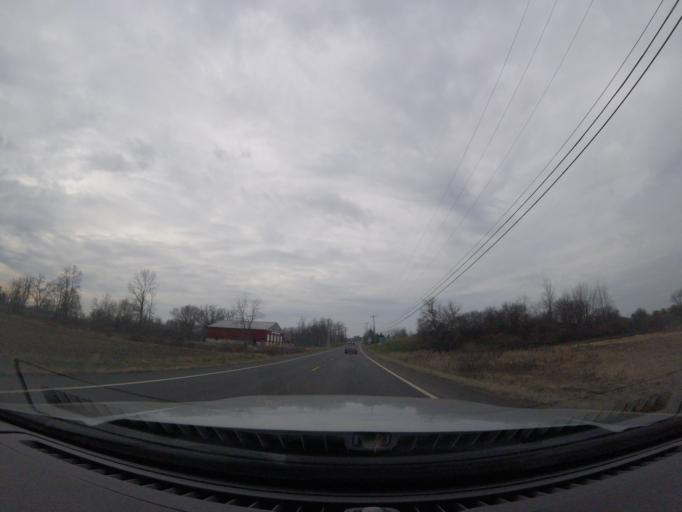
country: US
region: New York
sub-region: Schuyler County
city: Watkins Glen
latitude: 42.4220
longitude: -76.8359
